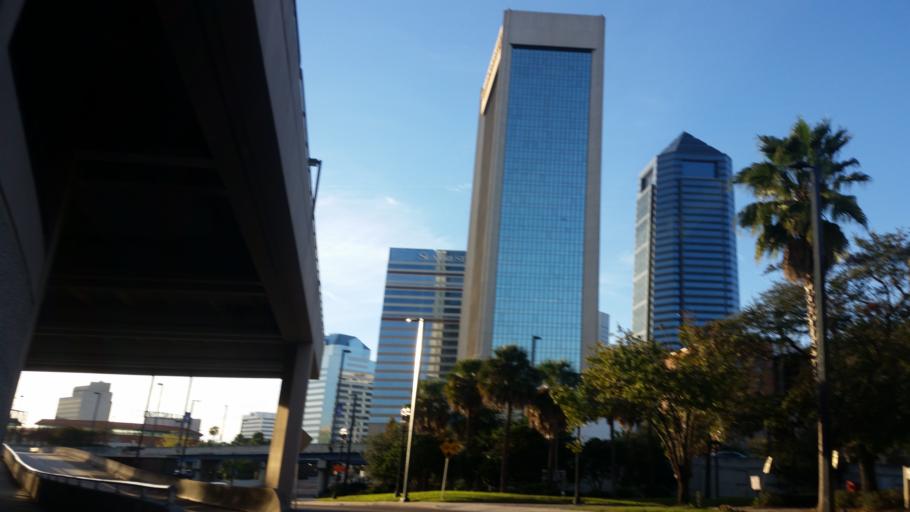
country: US
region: Florida
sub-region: Duval County
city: Jacksonville
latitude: 30.3250
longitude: -81.6565
